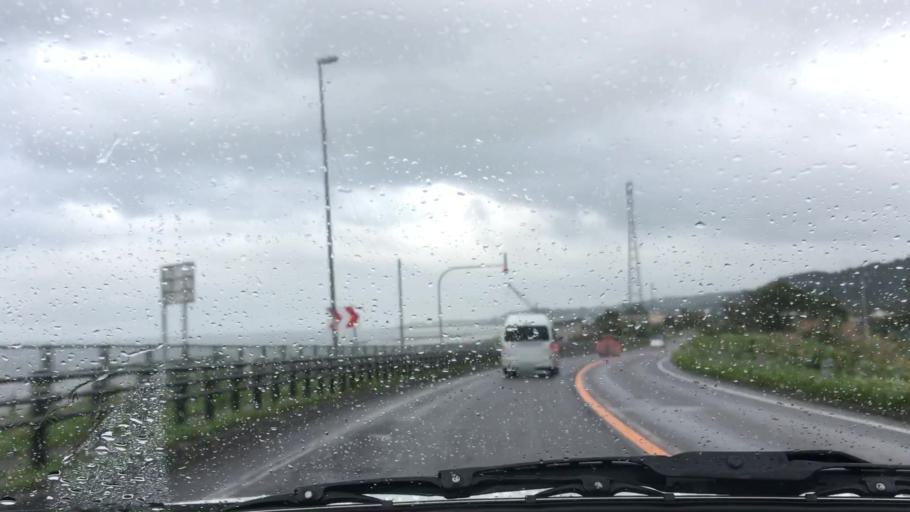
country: JP
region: Hokkaido
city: Nanae
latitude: 42.2343
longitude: 140.3212
